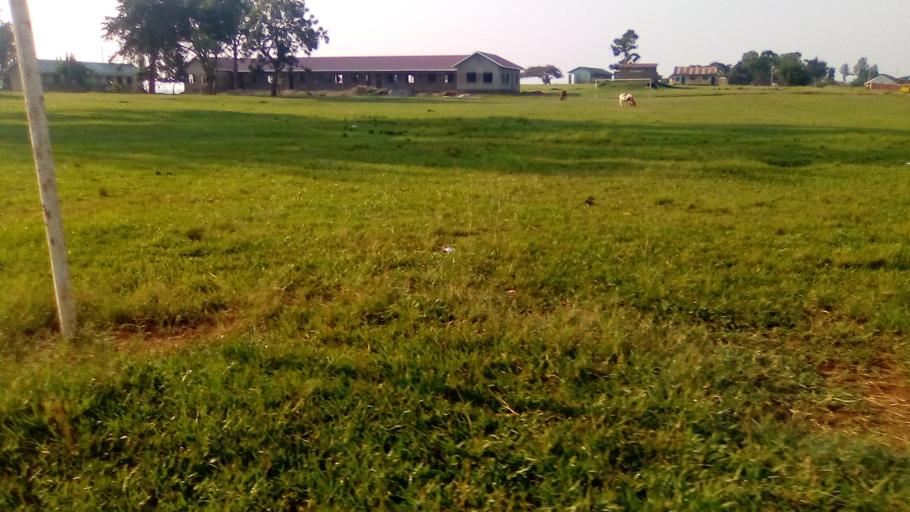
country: UG
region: Central Region
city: Masaka
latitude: -0.2747
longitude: 31.6441
